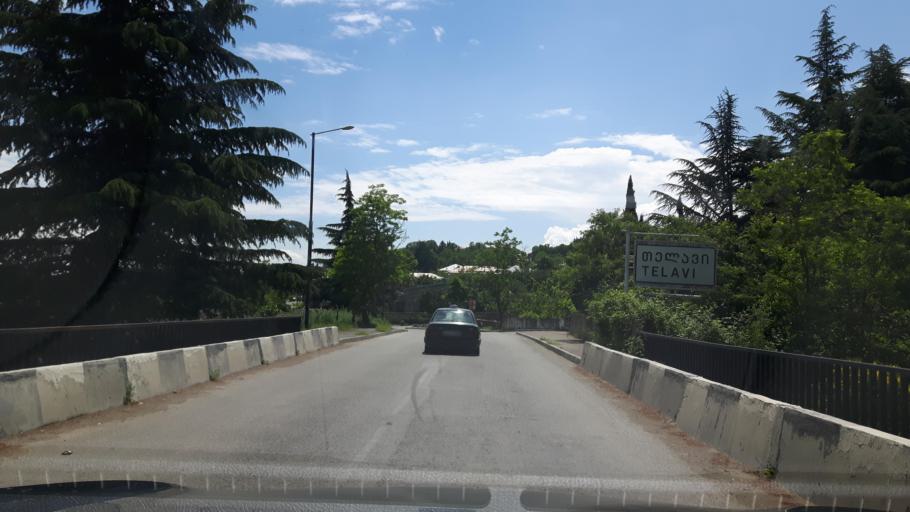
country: GE
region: Kakheti
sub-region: Telavi
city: Telavi
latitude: 41.9257
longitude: 45.4549
